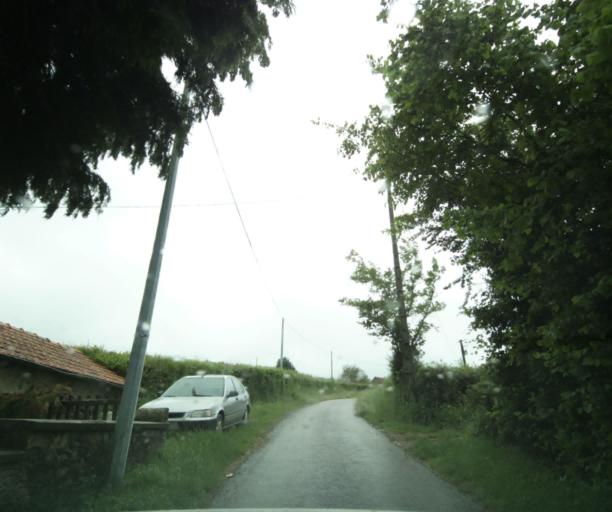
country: FR
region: Bourgogne
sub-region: Departement de Saone-et-Loire
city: Charolles
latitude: 46.4984
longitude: 4.3969
